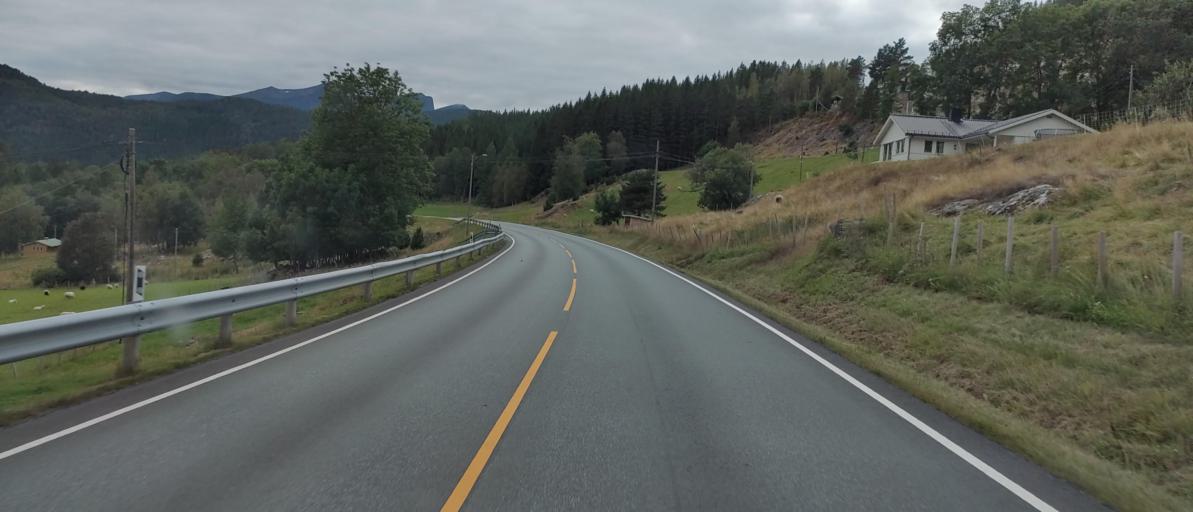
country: NO
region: More og Romsdal
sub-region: Rauma
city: Andalsnes
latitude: 62.5806
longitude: 7.5564
